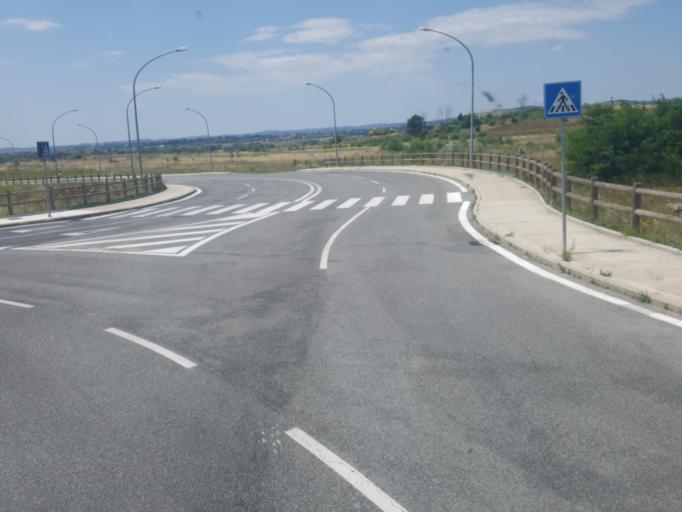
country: IT
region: Latium
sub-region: Citta metropolitana di Roma Capitale
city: Fiano Romano
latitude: 42.1661
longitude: 12.6496
